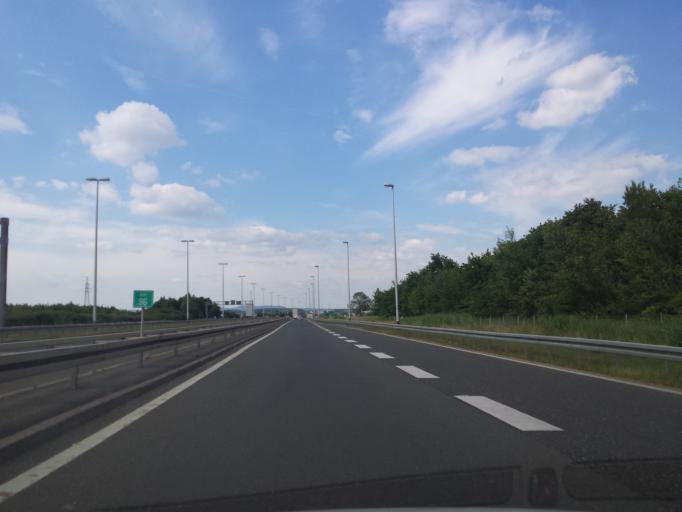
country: HR
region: Grad Zagreb
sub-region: Sesvete
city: Sesvete
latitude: 45.8052
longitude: 16.1328
